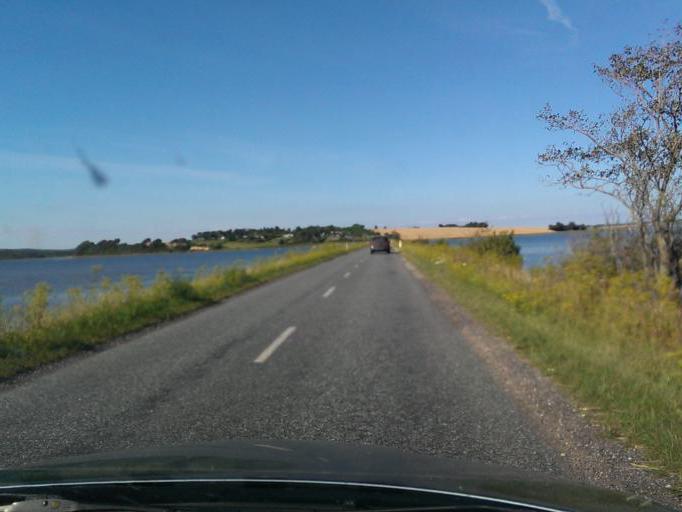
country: DK
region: Central Jutland
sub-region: Odder Kommune
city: Odder
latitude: 55.8643
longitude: 10.1157
